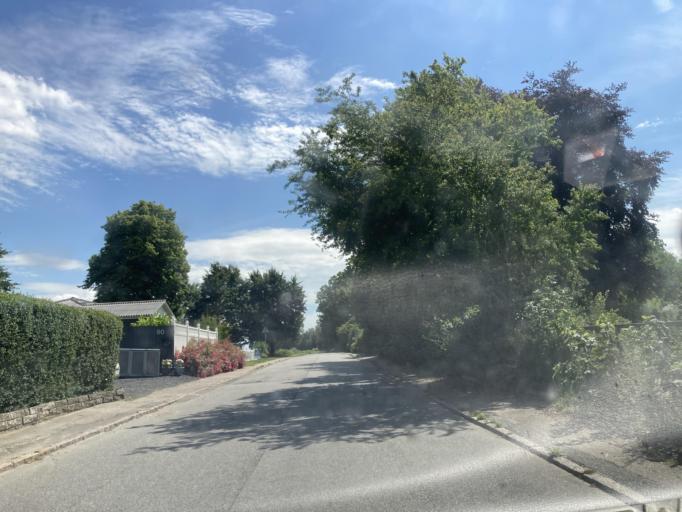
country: DK
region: Zealand
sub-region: Faxe Kommune
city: Haslev
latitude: 55.3860
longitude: 11.9380
